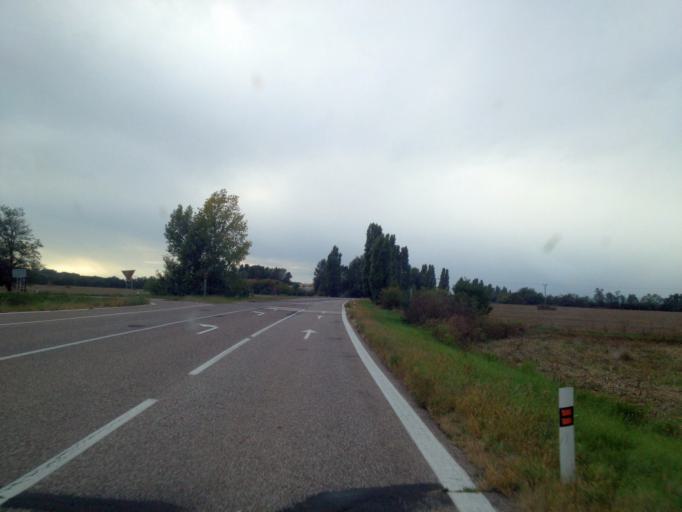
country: HU
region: Komarom-Esztergom
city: Sutto
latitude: 47.7692
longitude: 18.4761
